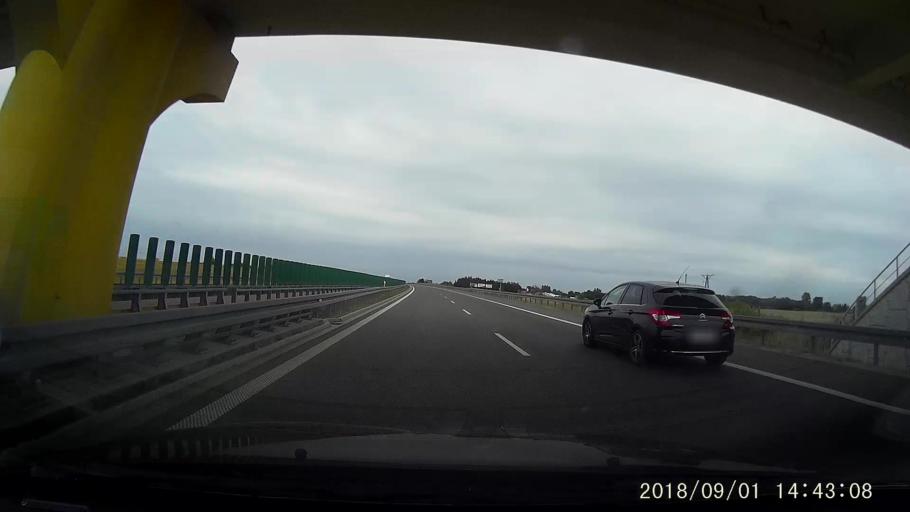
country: PL
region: Lubusz
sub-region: Powiat gorzowski
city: Jenin
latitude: 52.7630
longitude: 15.1338
